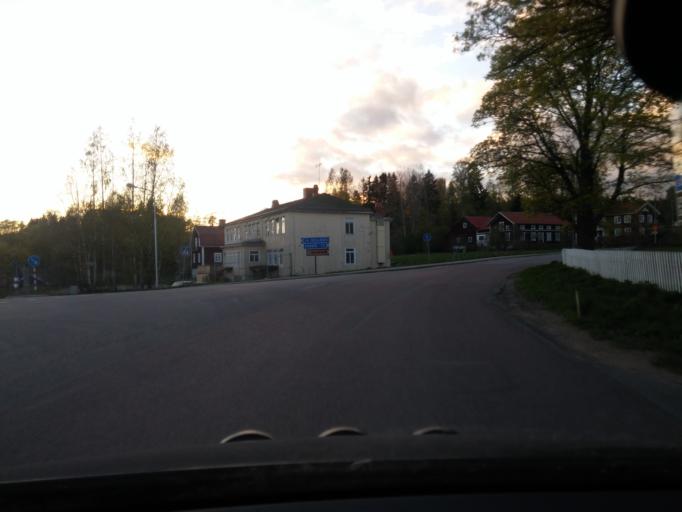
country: SE
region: Gaevleborg
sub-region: Bollnas Kommun
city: Bollnas
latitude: 61.4073
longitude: 16.5446
